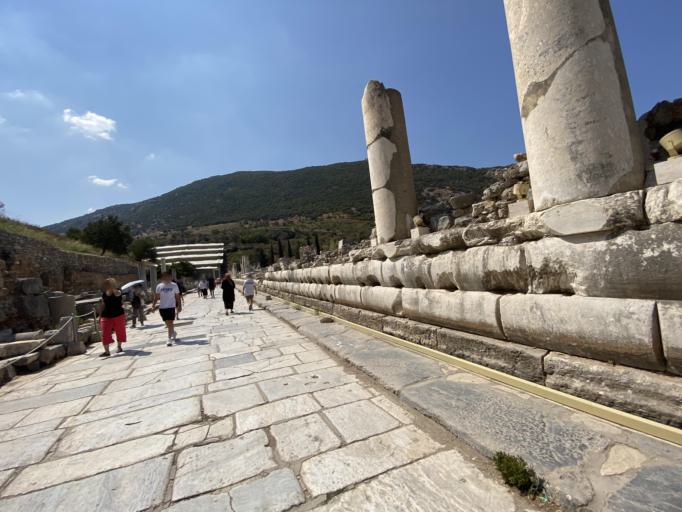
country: TR
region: Izmir
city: Selcuk
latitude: 37.9403
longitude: 27.3417
